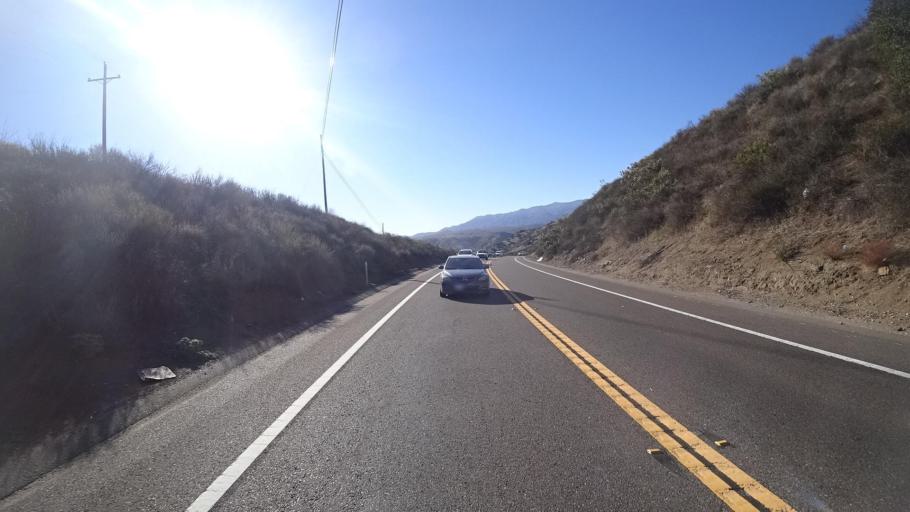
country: US
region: California
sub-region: San Diego County
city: Jamul
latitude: 32.6817
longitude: -116.8407
